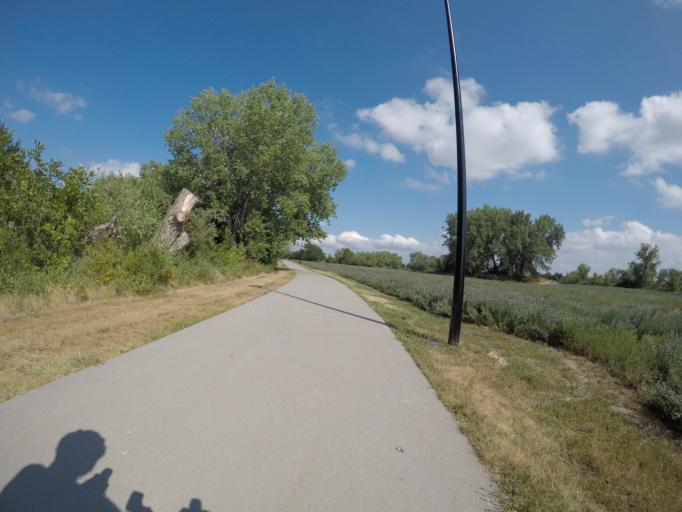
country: US
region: Nebraska
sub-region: Buffalo County
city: Kearney
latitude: 40.6740
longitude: -99.0521
